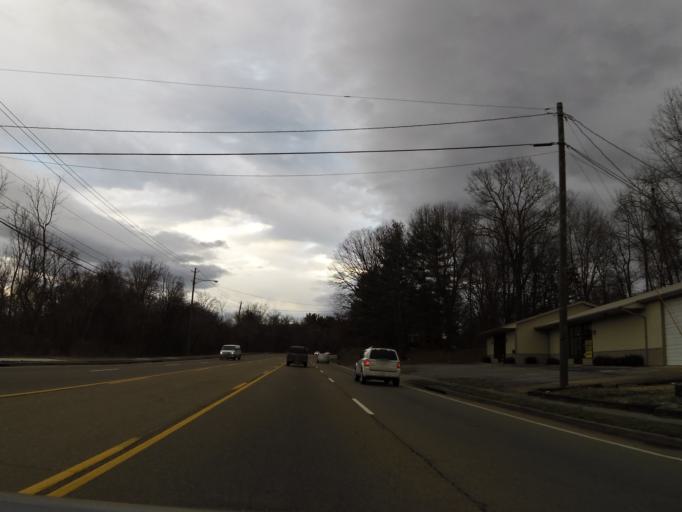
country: US
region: Tennessee
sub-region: Carter County
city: Central
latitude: 36.3400
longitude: -82.2569
